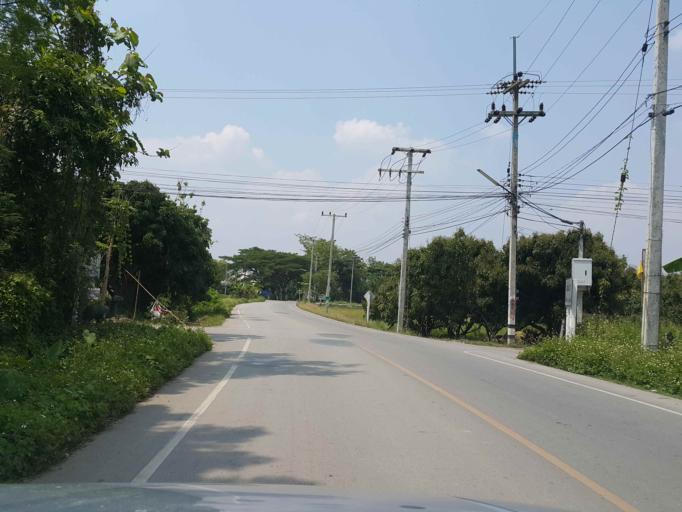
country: TH
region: Chiang Mai
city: Hang Dong
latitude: 18.7011
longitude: 98.9652
